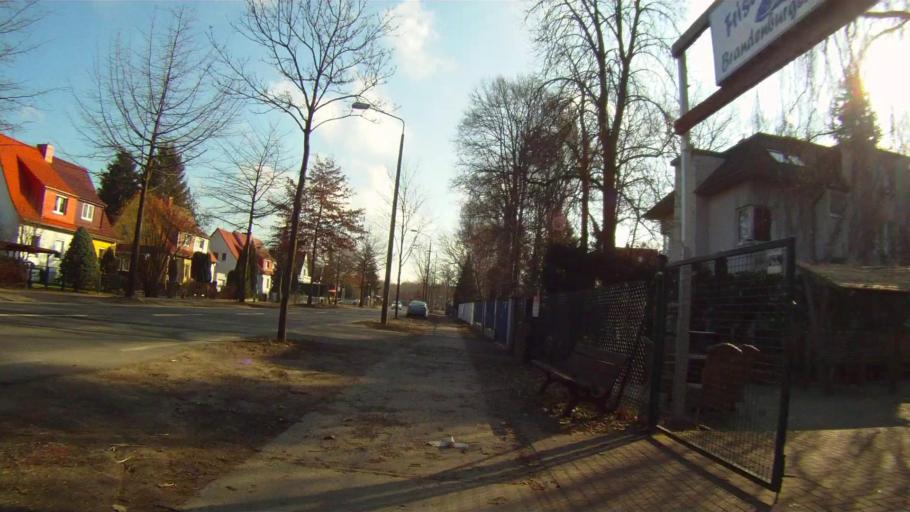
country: DE
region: Berlin
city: Rahnsdorf
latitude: 52.4326
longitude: 13.7116
